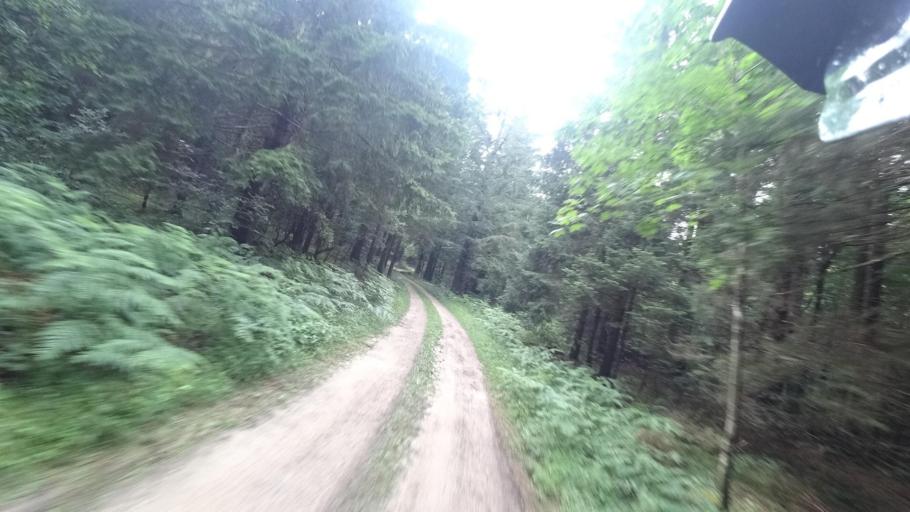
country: HR
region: Licko-Senjska
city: Jezerce
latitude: 44.7793
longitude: 15.6457
